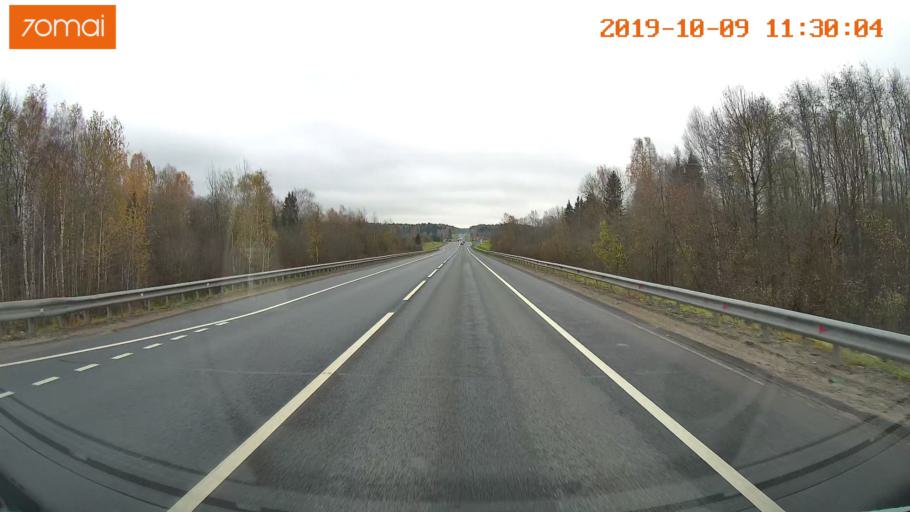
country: RU
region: Vologda
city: Vologda
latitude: 59.0570
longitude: 40.0671
